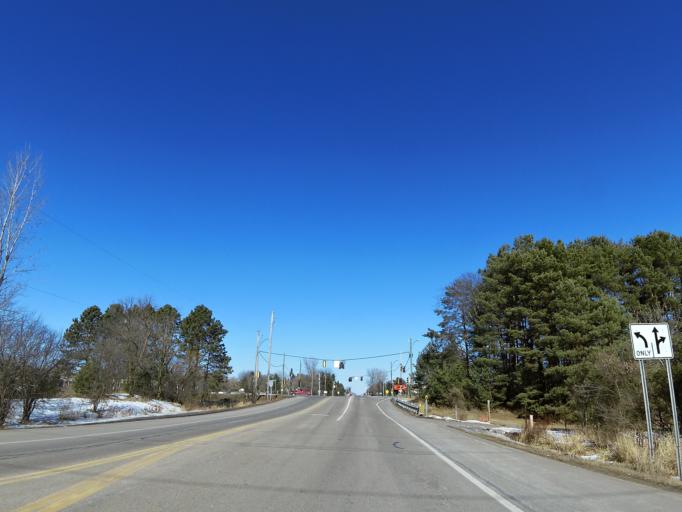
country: US
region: Minnesota
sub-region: Washington County
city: Lake Elmo
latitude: 45.0345
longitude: -92.8834
